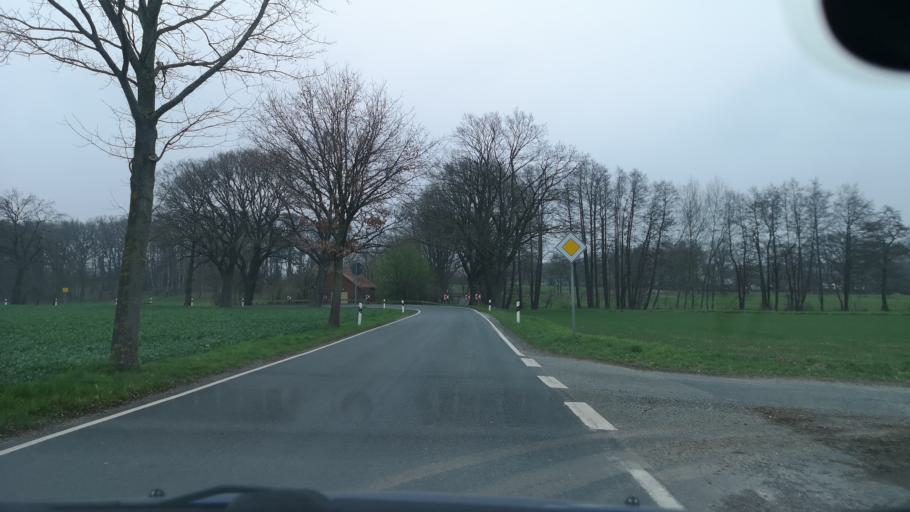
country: DE
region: Lower Saxony
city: Neustadt am Rubenberge
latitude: 52.5725
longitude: 9.4428
